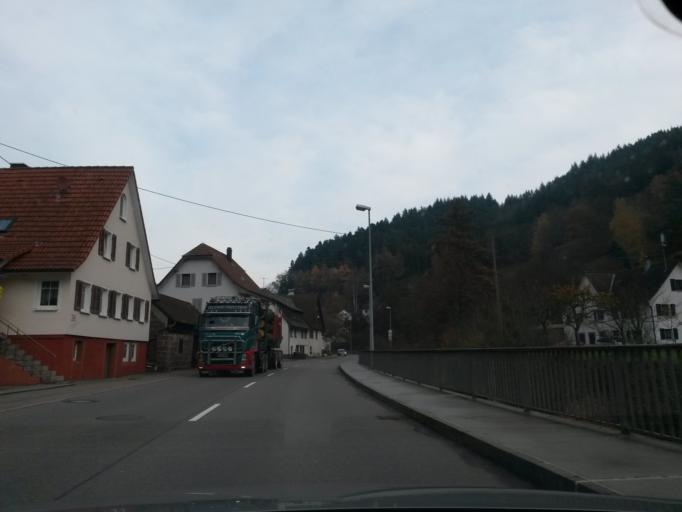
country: DE
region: Baden-Wuerttemberg
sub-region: Karlsruhe Region
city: Alpirsbach
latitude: 48.3366
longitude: 8.3947
